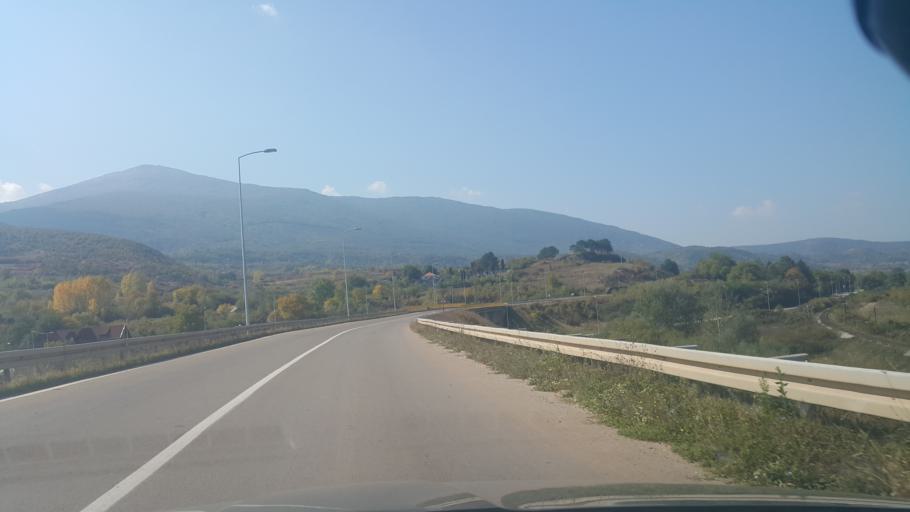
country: RS
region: Central Serbia
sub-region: Pirotski Okrug
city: Bela Palanka
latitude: 43.2228
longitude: 22.3016
